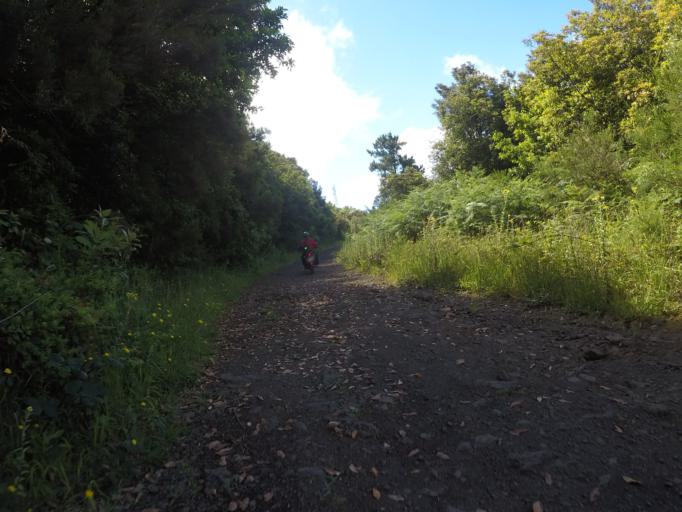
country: PT
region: Madeira
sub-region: Sao Vicente
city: Sao Vicente
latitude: 32.7744
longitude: -17.0535
